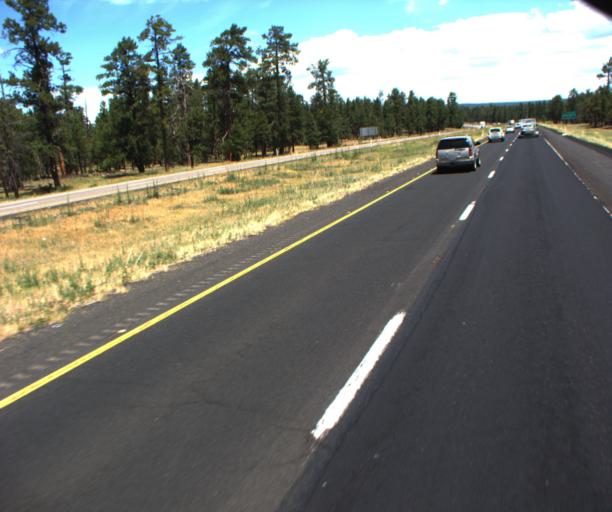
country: US
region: Arizona
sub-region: Coconino County
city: Sedona
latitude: 34.8390
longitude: -111.6041
